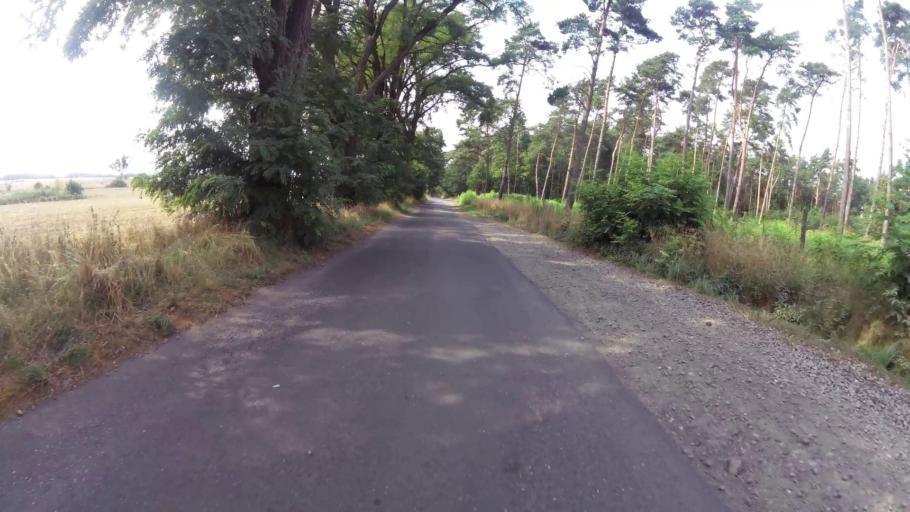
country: PL
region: West Pomeranian Voivodeship
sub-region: Powiat gryfinski
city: Mieszkowice
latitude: 52.8719
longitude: 14.5178
